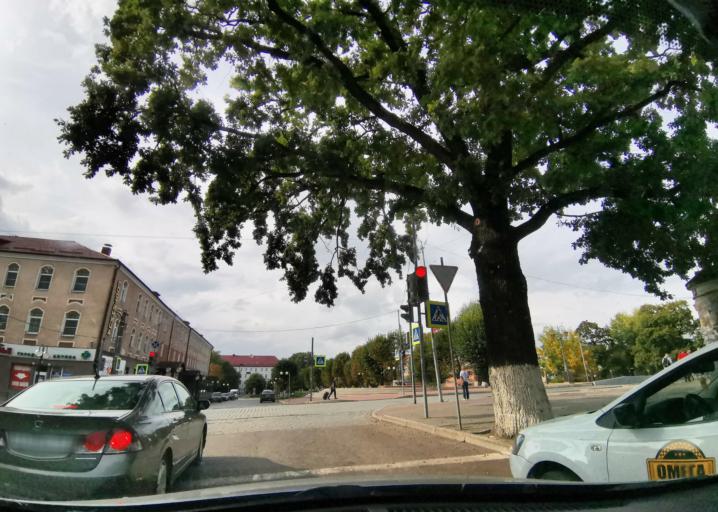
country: RU
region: Kaliningrad
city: Gusev
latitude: 54.5902
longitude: 22.2000
